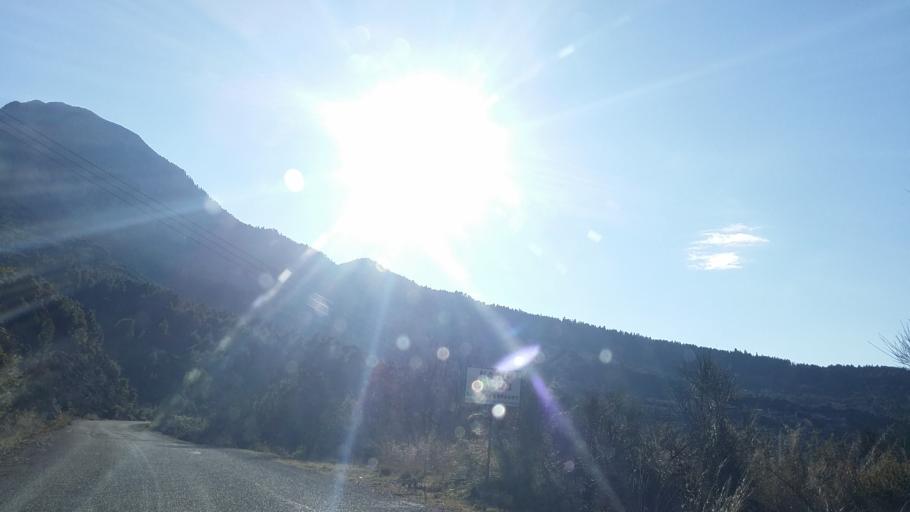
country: GR
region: Central Greece
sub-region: Nomos Evrytanias
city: Kerasochori
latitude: 38.8792
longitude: 21.5796
